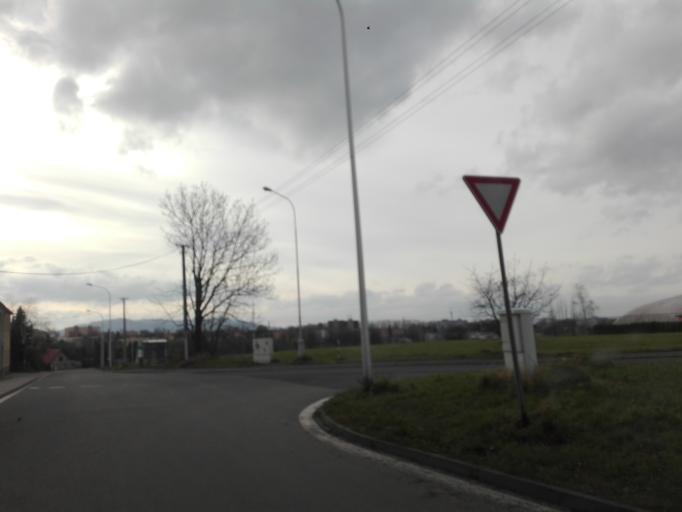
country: CZ
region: Moravskoslezsky
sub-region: Okres Frydek-Mistek
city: Frydek-Mistek
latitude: 49.6974
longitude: 18.3497
